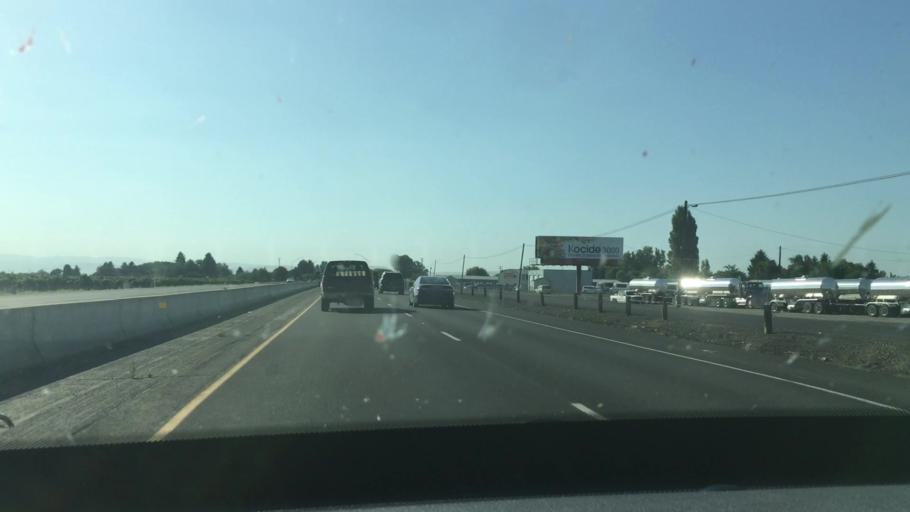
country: US
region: Washington
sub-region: Yakima County
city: Toppenish
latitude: 46.3870
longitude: -120.3530
